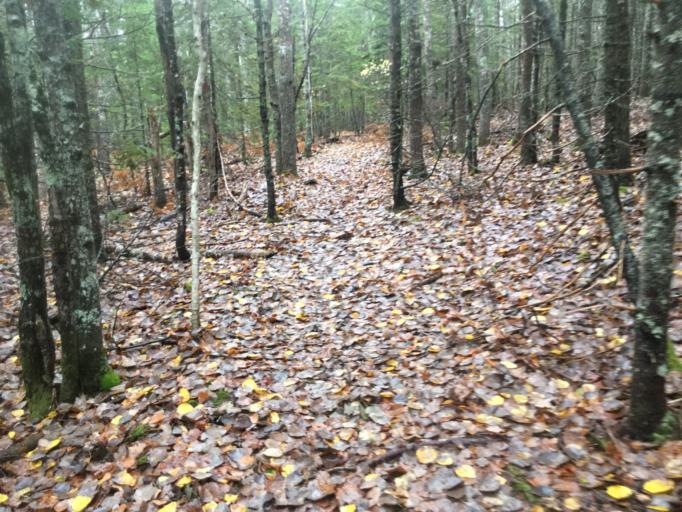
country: CA
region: Nova Scotia
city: New Glasgow
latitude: 45.5517
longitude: -62.6810
